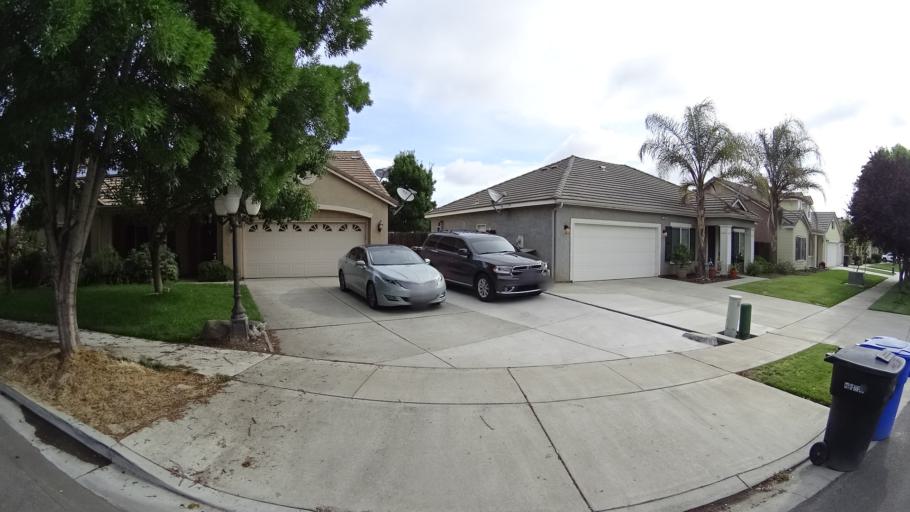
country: US
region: California
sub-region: Kings County
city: Hanford
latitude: 36.3342
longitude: -119.6749
